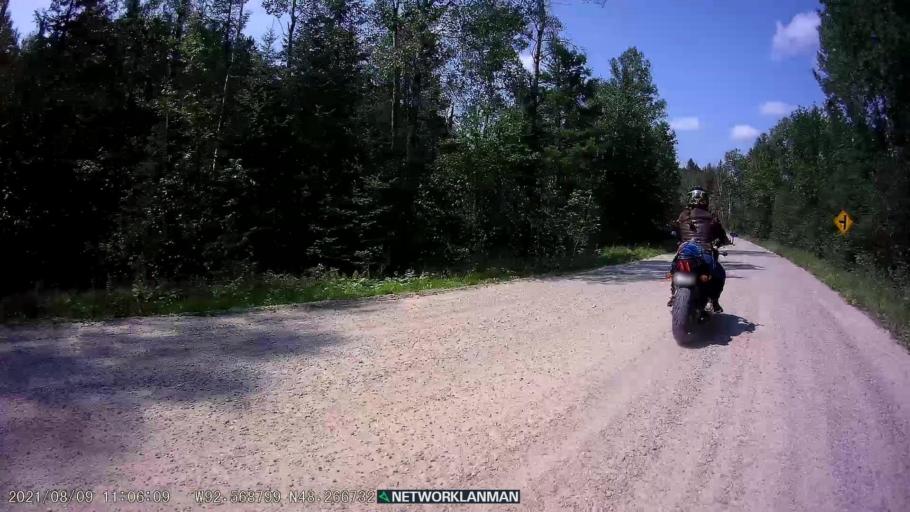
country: US
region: Minnesota
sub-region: Saint Louis County
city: Parkville
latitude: 48.2668
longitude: -92.5691
